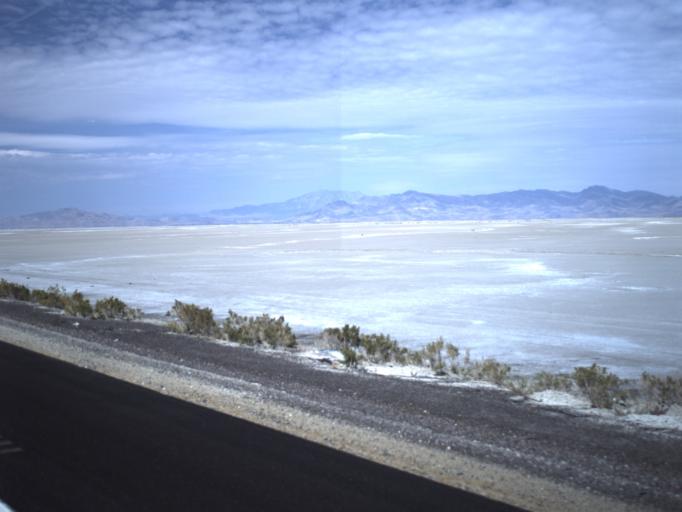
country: US
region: Utah
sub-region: Tooele County
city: Wendover
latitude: 40.7338
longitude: -113.5843
